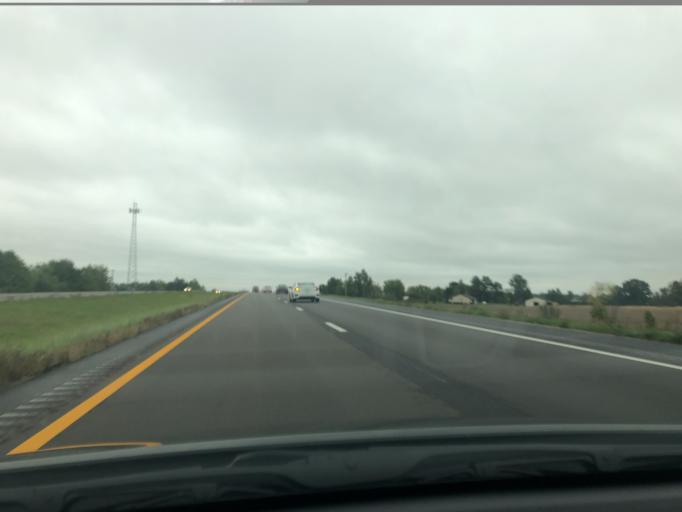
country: US
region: Ohio
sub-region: Union County
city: Marysville
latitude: 40.2534
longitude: -83.4444
